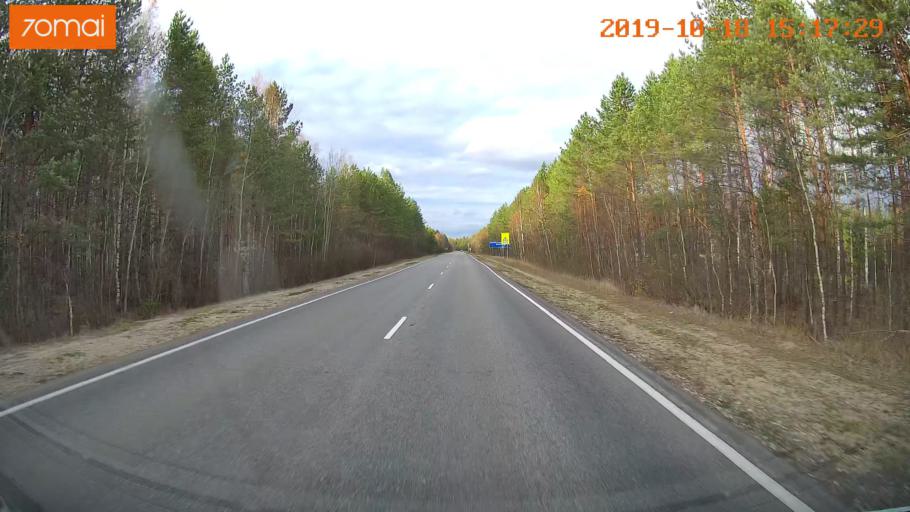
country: RU
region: Vladimir
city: Anopino
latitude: 55.6504
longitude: 40.7266
